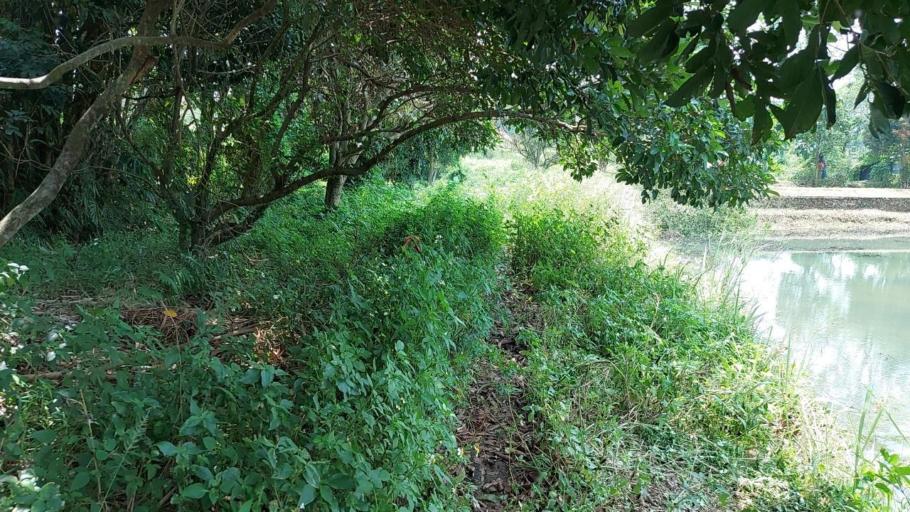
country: ID
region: West Java
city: Cibinong
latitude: -6.4905
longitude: 106.8510
